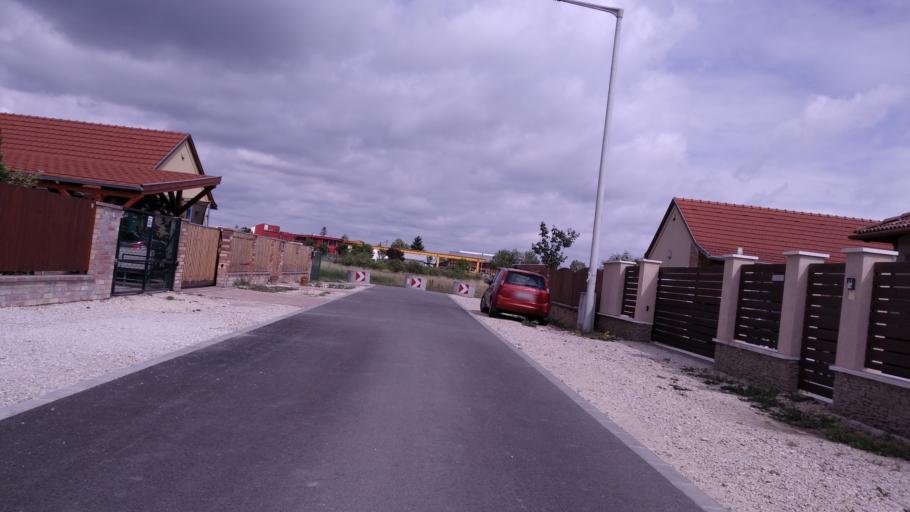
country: HU
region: Pest
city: Budakalasz
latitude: 47.6222
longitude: 19.0579
